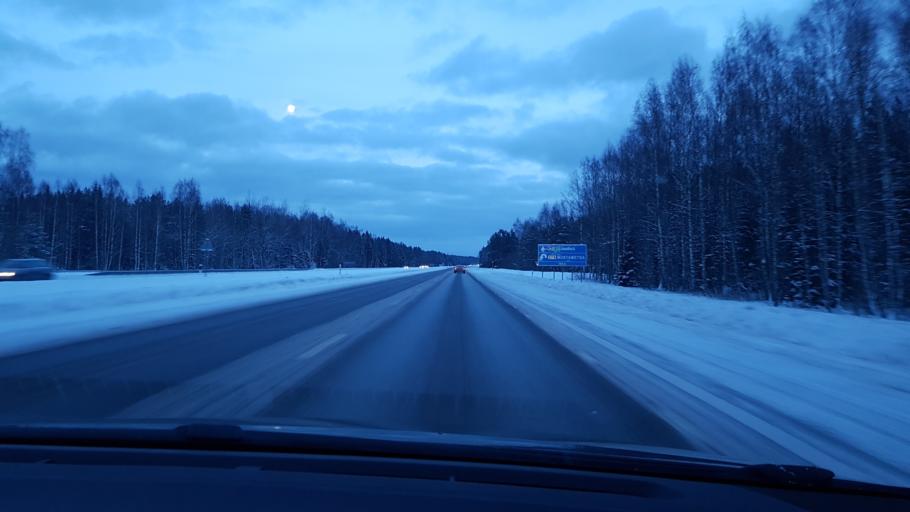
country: EE
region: Harju
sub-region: Kuusalu vald
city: Kuusalu
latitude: 59.4607
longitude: 25.5948
